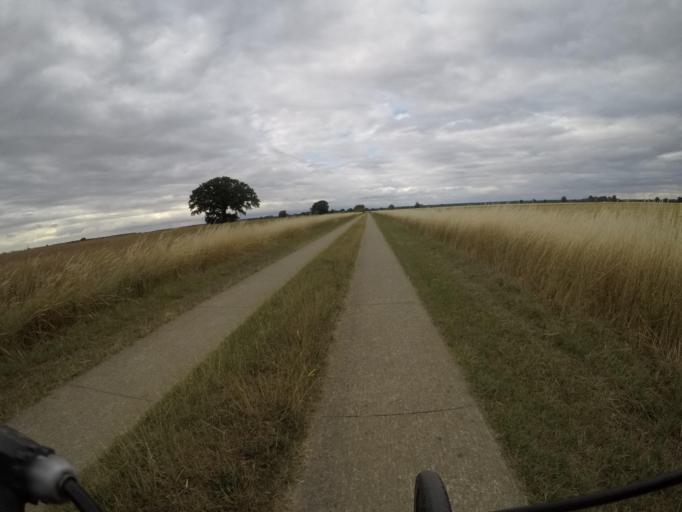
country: DE
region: Lower Saxony
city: Neu Darchau
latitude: 53.2438
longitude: 10.9122
